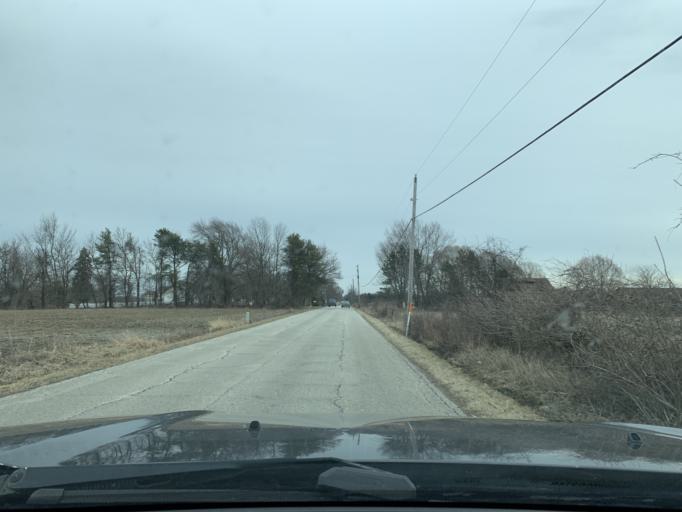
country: US
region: Indiana
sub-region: Porter County
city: Chesterton
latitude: 41.5862
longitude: -87.0247
